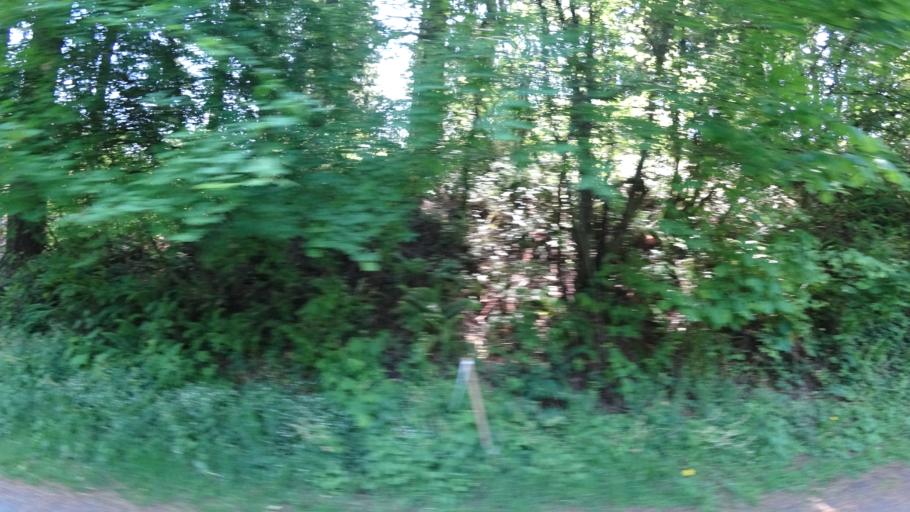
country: US
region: Oregon
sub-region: Multnomah County
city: Portland
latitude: 45.5149
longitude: -122.7168
